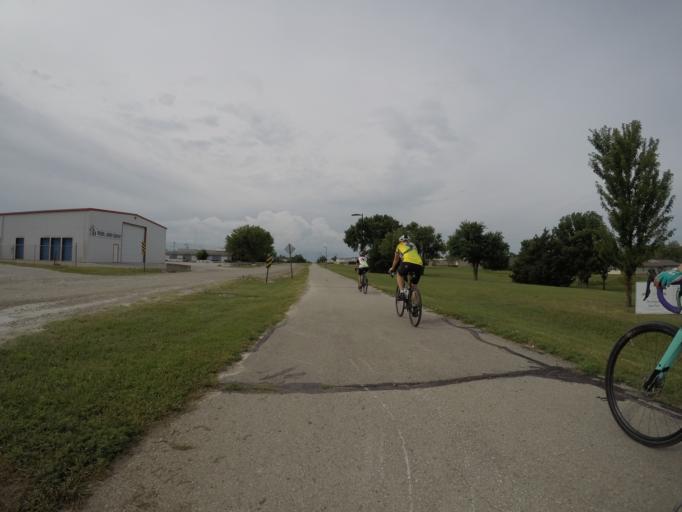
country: US
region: Kansas
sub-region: Franklin County
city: Ottawa
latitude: 38.5937
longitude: -95.2704
